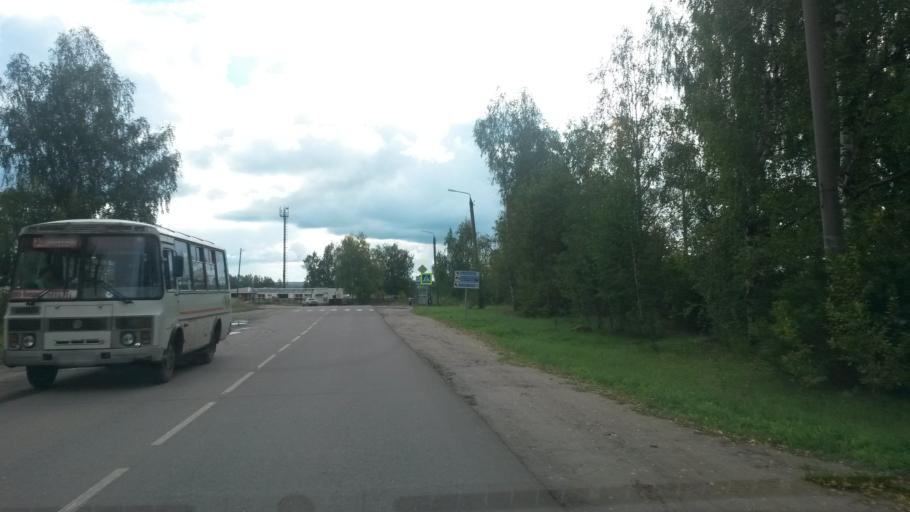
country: RU
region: Ivanovo
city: Zavolzhsk
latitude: 57.4674
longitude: 42.1624
